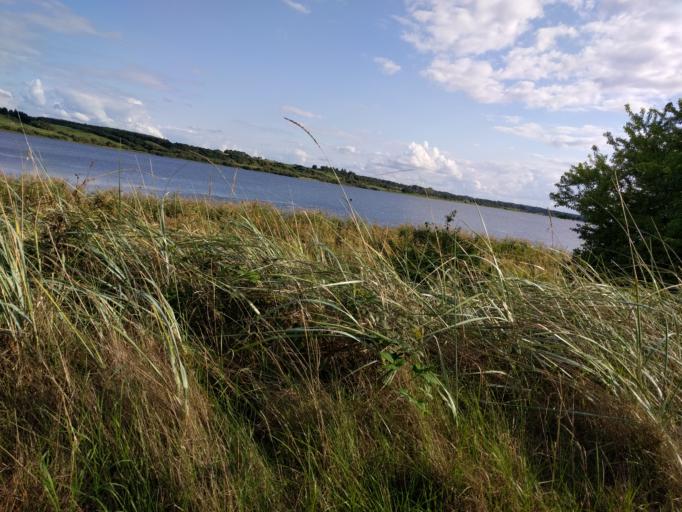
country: DK
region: Central Jutland
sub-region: Skive Kommune
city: Hojslev
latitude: 56.6019
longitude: 9.2877
